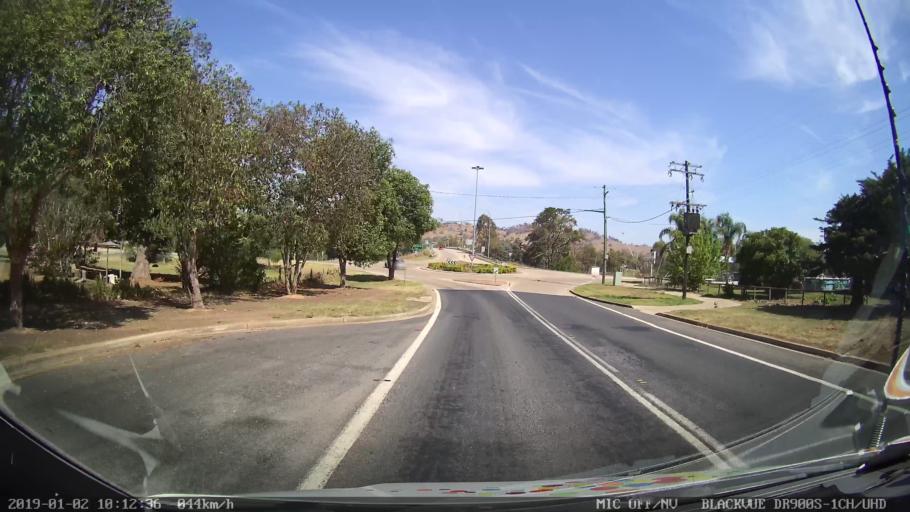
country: AU
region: New South Wales
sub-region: Gundagai
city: Gundagai
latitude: -35.0841
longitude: 148.0942
